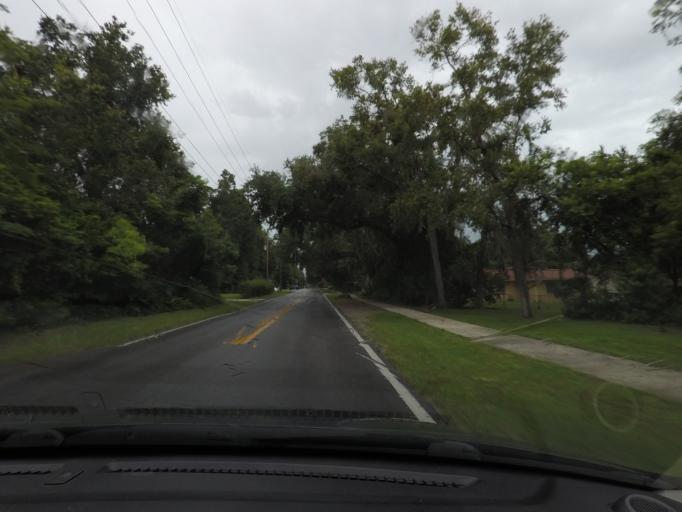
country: US
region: Florida
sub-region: Orange County
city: Conway
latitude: 28.4976
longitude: -81.3391
